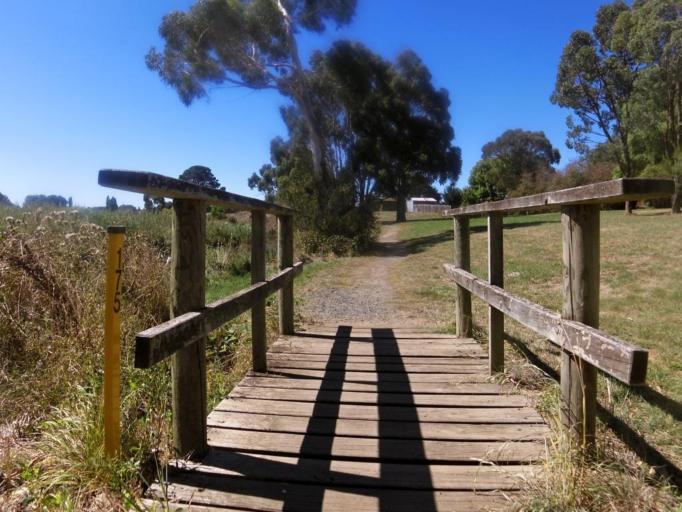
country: AU
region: Victoria
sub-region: Mount Alexander
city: Castlemaine
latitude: -37.2481
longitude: 144.4419
